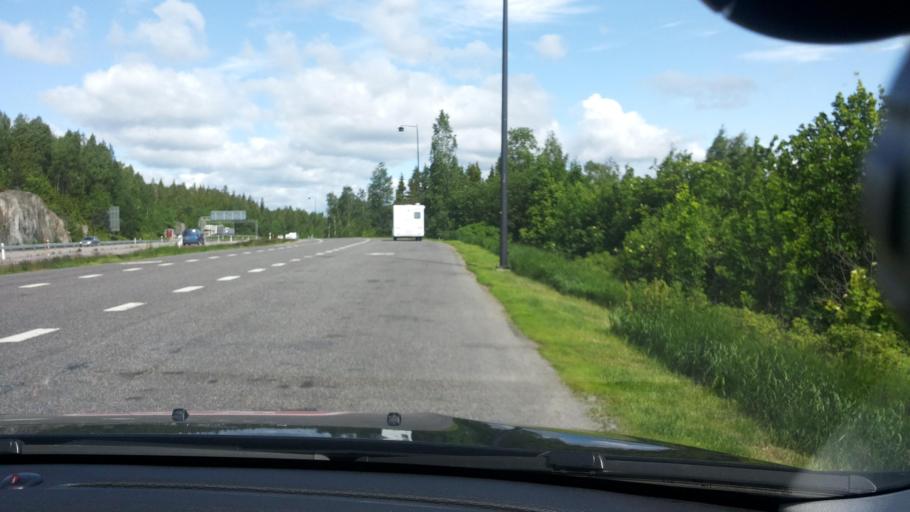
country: SE
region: Vaesternorrland
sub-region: Sundsvalls Kommun
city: Sundsbruk
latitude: 62.4575
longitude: 17.3449
